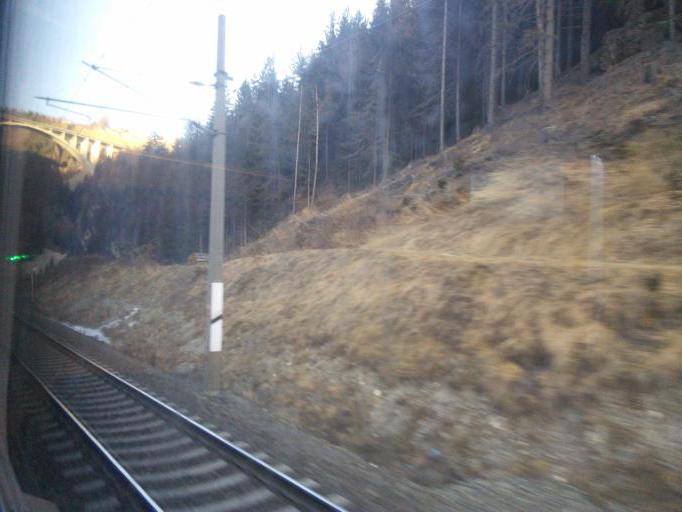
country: AT
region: Tyrol
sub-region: Politischer Bezirk Innsbruck Land
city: Gries am Brenner
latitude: 47.0647
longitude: 11.4907
